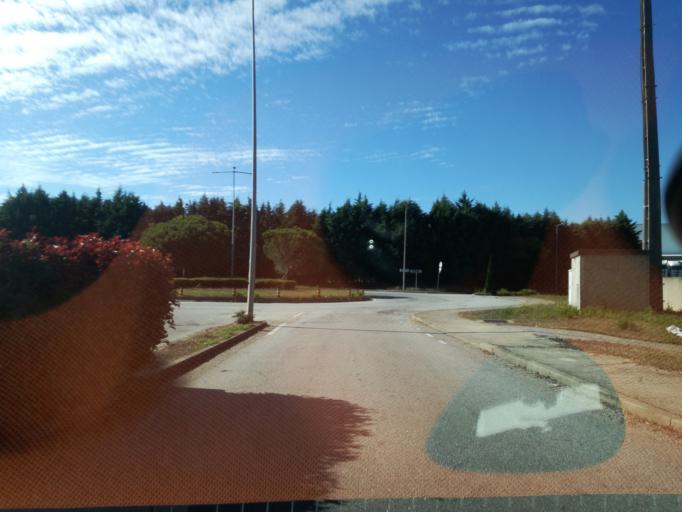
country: PT
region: Porto
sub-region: Pacos de Ferreira
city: Seroa
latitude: 41.2592
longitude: -8.4446
